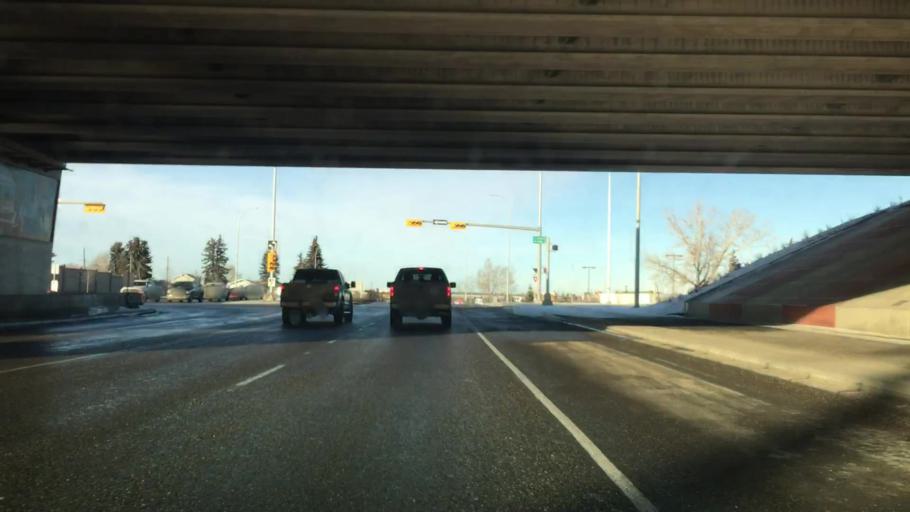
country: CA
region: Alberta
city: Calgary
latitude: 50.9790
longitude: -113.9986
